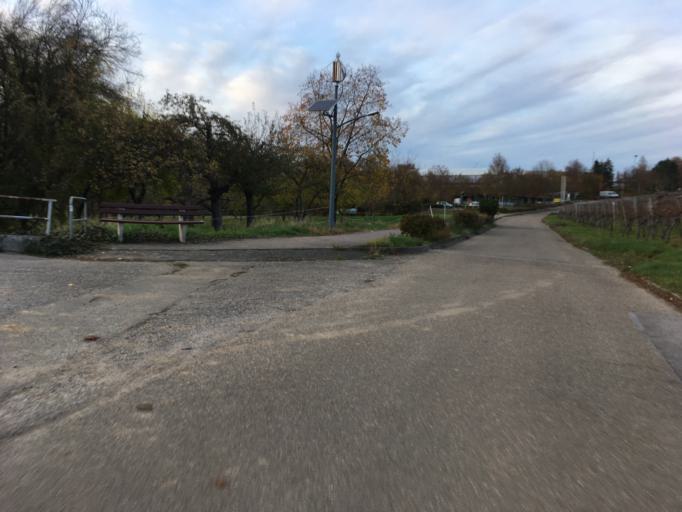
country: DE
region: Baden-Wuerttemberg
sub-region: Regierungsbezirk Stuttgart
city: Neckarwestheim
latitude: 49.0407
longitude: 9.1888
